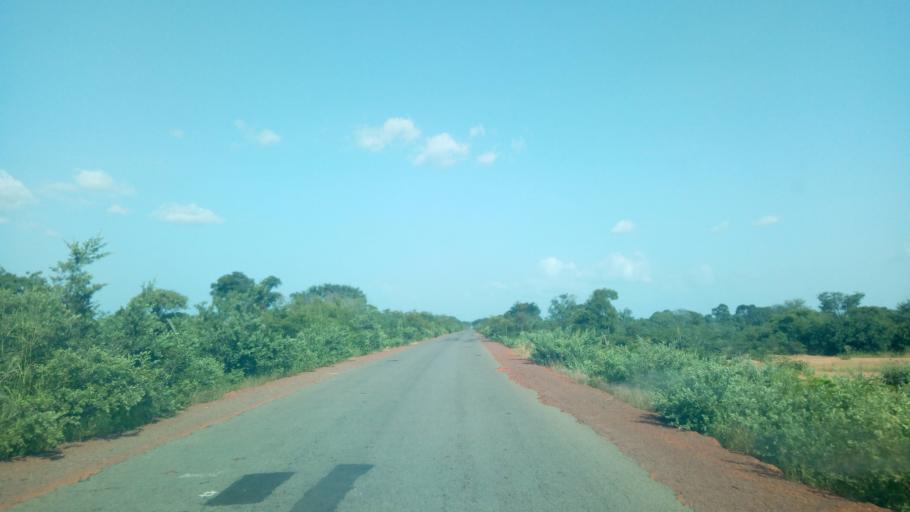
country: ML
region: Sikasso
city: Yorosso
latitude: 12.2120
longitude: -4.8996
